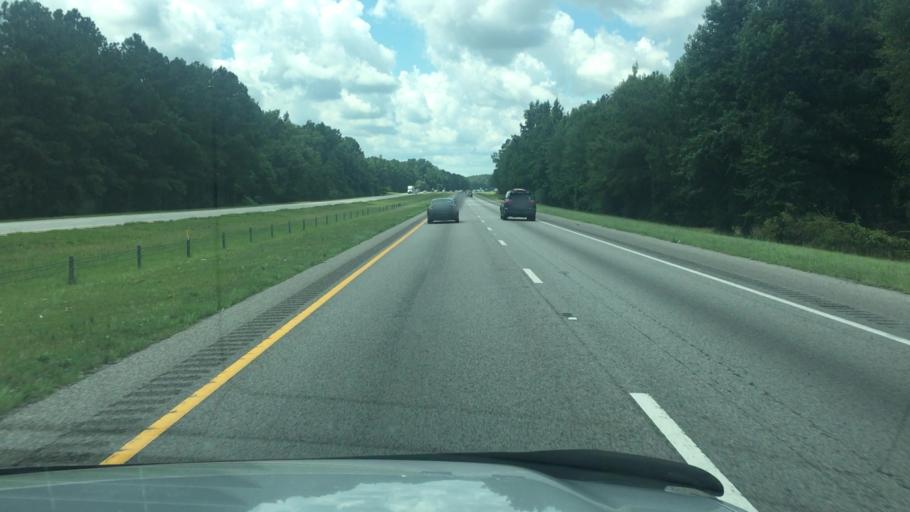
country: US
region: South Carolina
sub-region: Kershaw County
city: Lugoff
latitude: 34.2091
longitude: -80.6486
